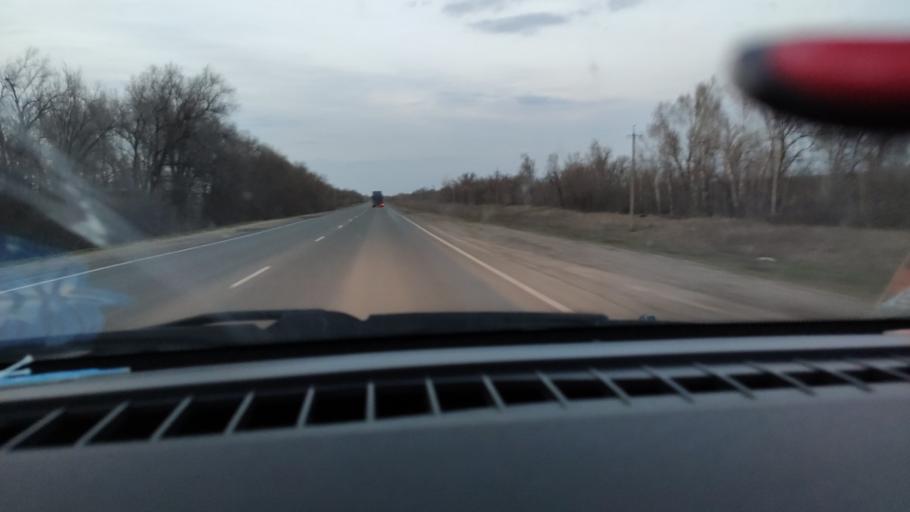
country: RU
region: Saratov
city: Sinodskoye
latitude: 52.0313
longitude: 46.7226
